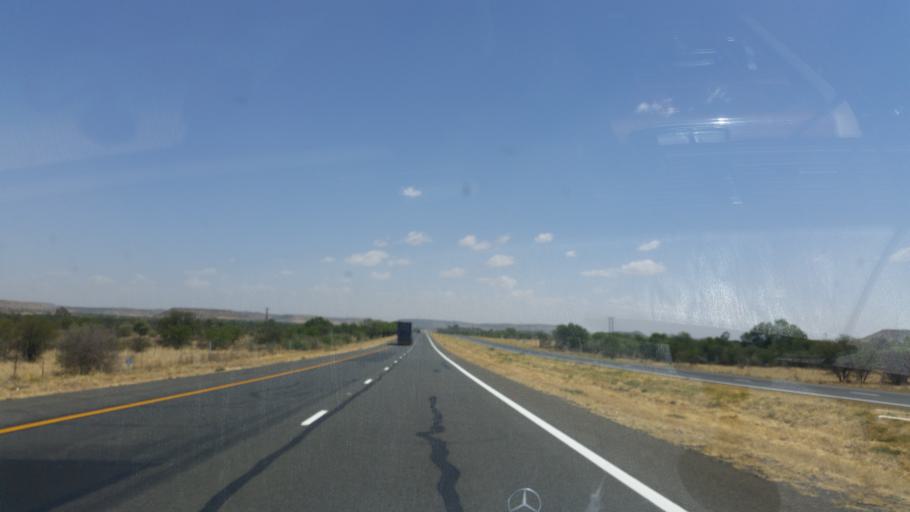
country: ZA
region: Orange Free State
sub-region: Mangaung Metropolitan Municipality
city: Bloemfontein
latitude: -28.9572
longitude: 26.3766
